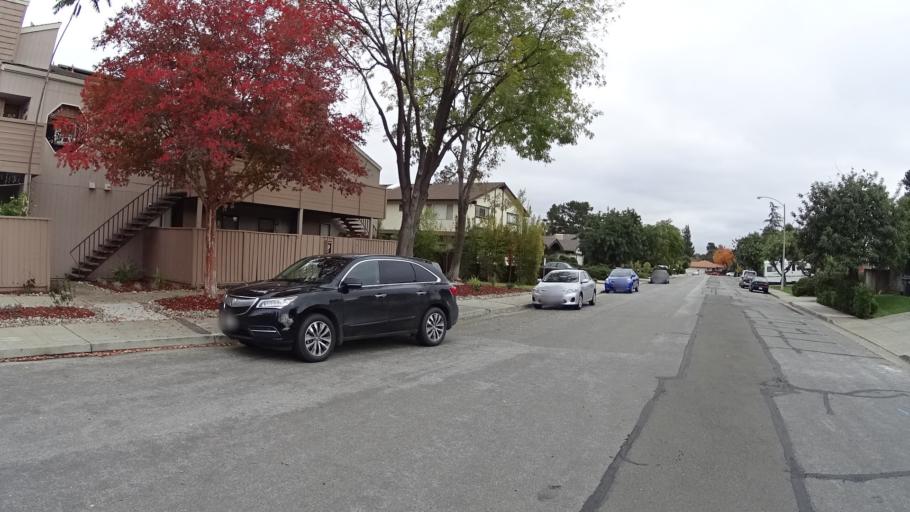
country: US
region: California
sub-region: Santa Clara County
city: Sunnyvale
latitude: 37.3551
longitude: -122.0302
